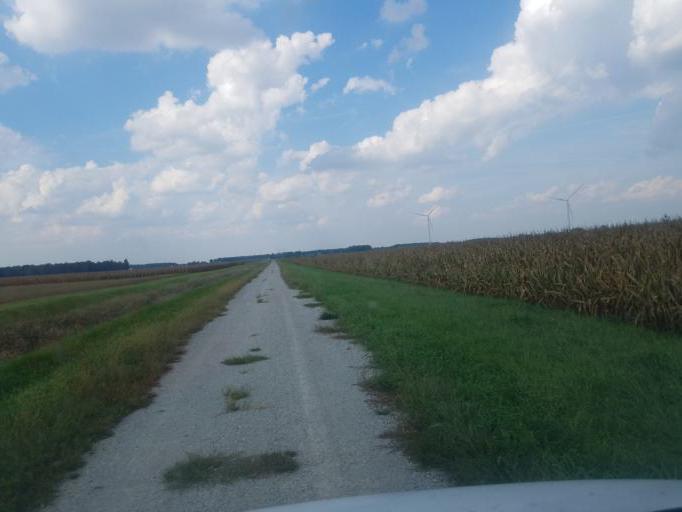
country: US
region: Ohio
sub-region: Hancock County
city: Arlington
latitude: 40.7915
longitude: -83.6899
